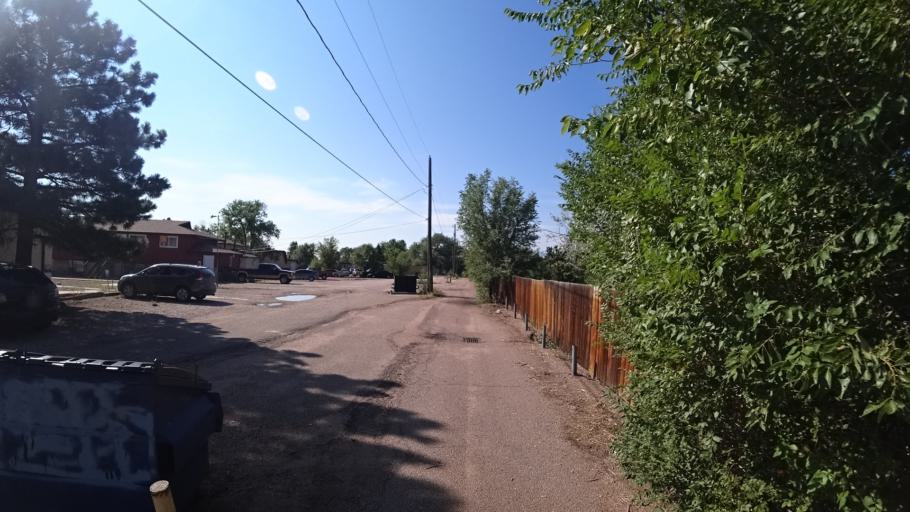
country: US
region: Colorado
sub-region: El Paso County
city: Colorado Springs
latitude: 38.8943
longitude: -104.8448
